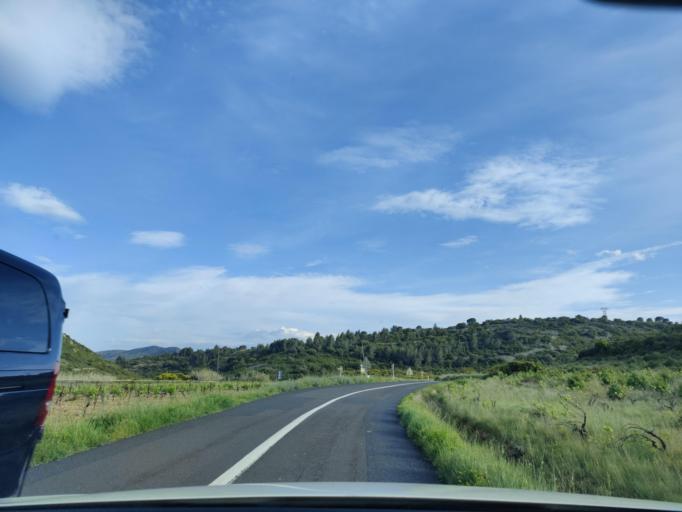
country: FR
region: Languedoc-Roussillon
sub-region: Departement des Pyrenees-Orientales
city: Estagel
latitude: 42.7936
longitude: 2.6987
